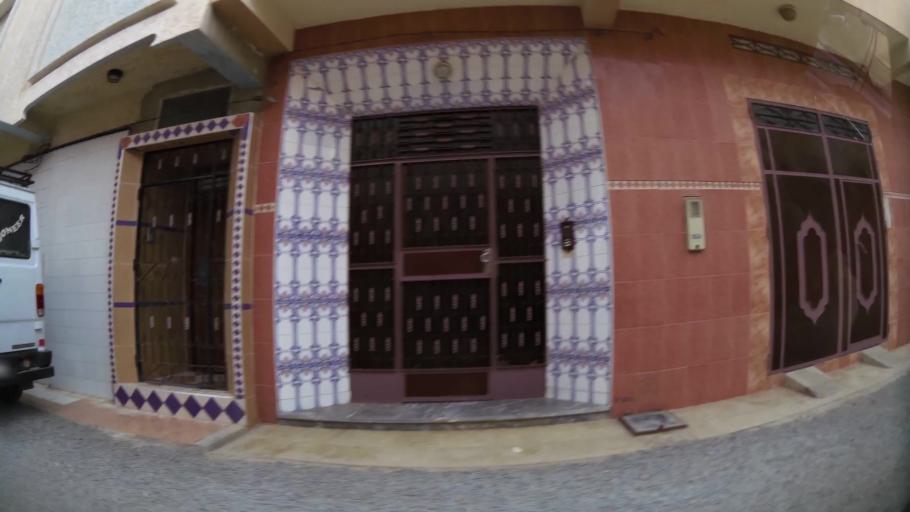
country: MA
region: Oriental
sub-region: Nador
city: Nador
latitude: 35.1588
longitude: -2.9367
